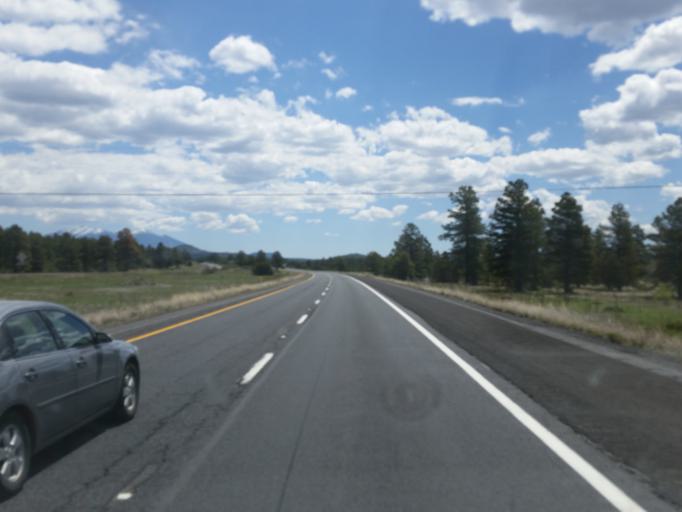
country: US
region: Arizona
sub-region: Coconino County
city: Parks
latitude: 35.2473
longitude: -111.9765
